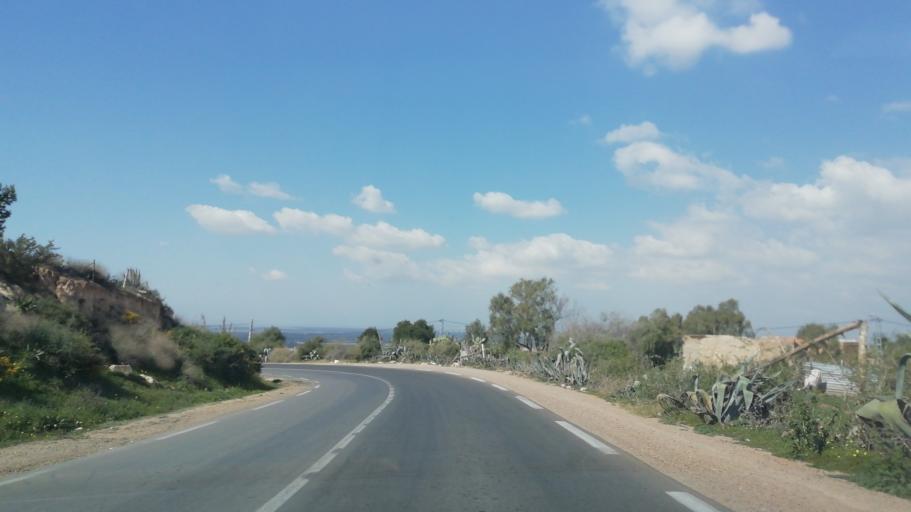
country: DZ
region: Mascara
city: Mascara
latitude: 35.5569
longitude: 0.0777
